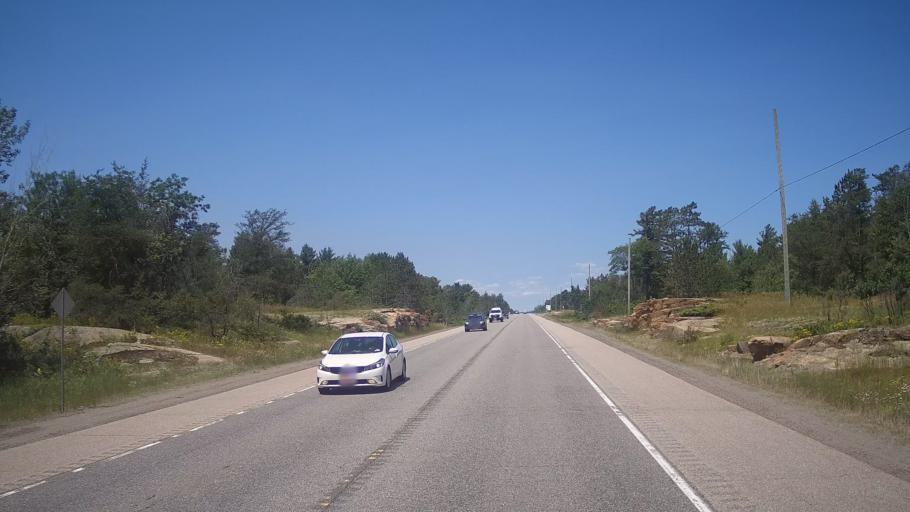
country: CA
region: Ontario
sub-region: Parry Sound District
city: Parry Sound
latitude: 45.6969
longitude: -80.4536
